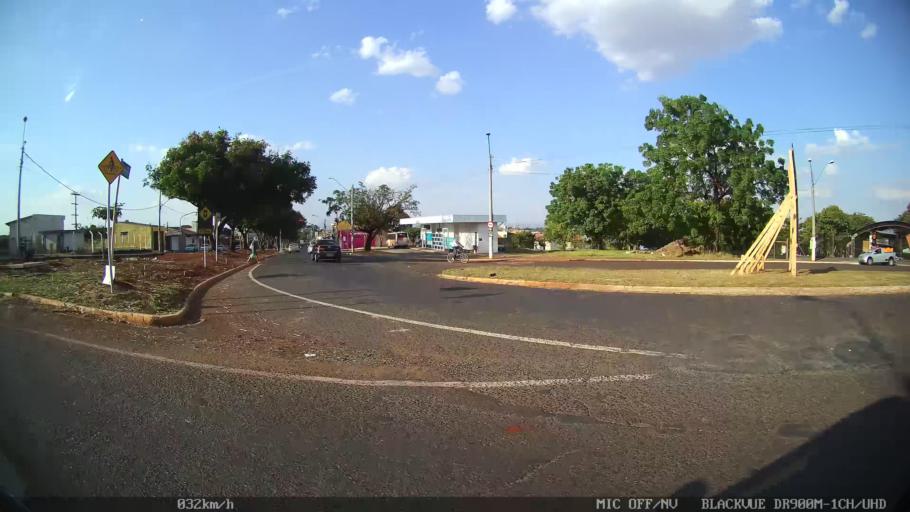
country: BR
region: Sao Paulo
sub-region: Ribeirao Preto
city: Ribeirao Preto
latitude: -21.1390
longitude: -47.8339
